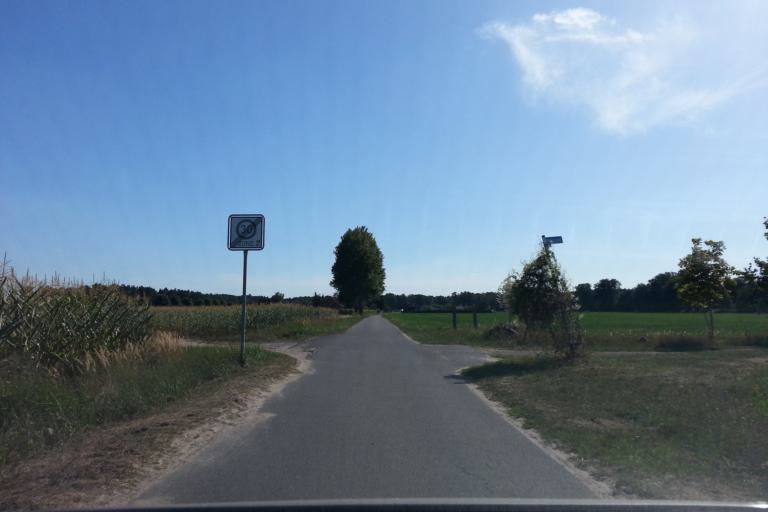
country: DE
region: Mecklenburg-Vorpommern
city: Eggesin
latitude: 53.6823
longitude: 14.0383
